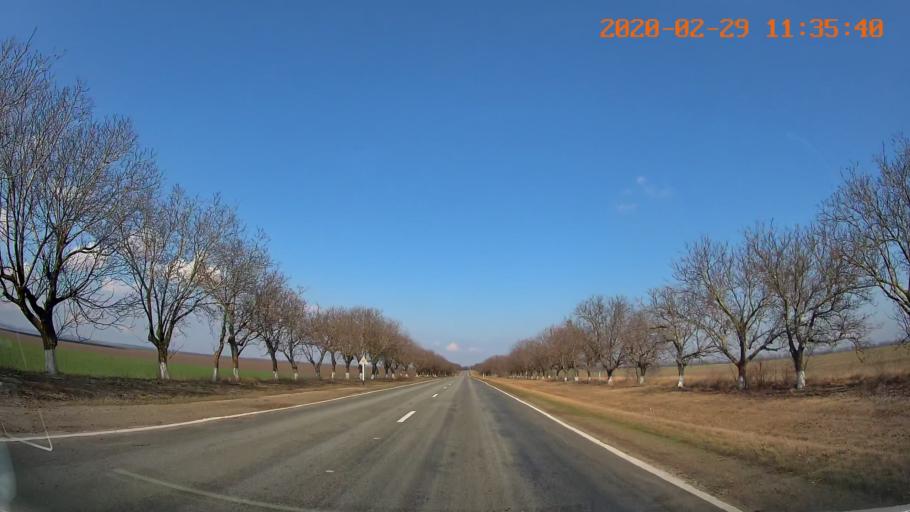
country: MD
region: Rezina
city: Saharna
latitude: 47.5841
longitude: 29.0618
